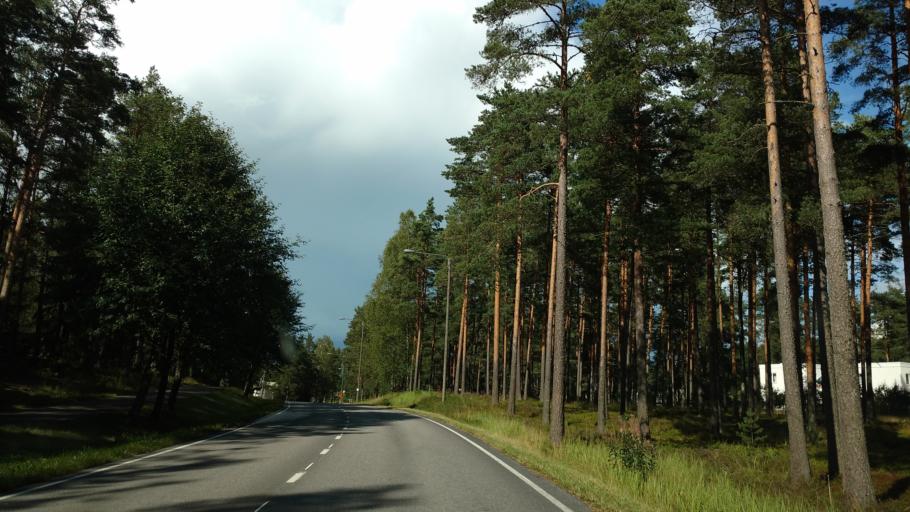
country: FI
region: Varsinais-Suomi
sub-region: Turku
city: Paimio
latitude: 60.4638
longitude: 22.7320
